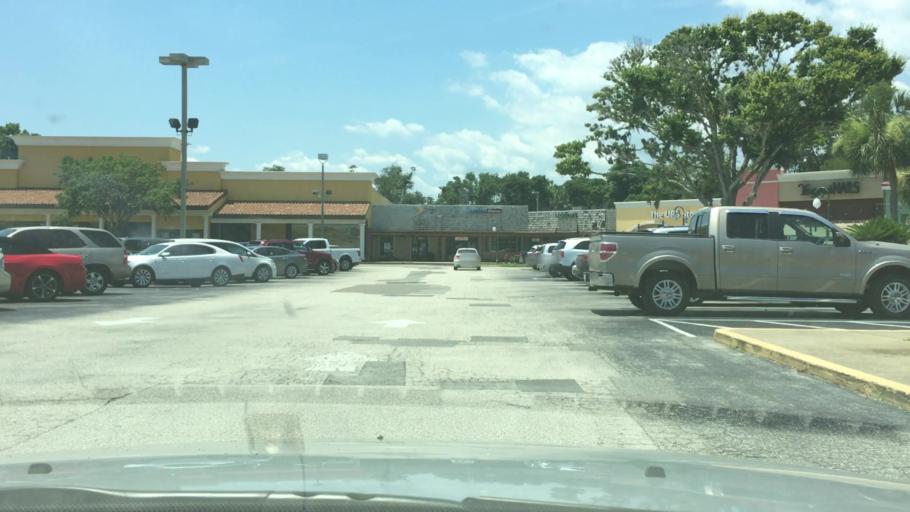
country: US
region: Florida
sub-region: Volusia County
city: Ormond Beach
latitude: 29.2837
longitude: -81.0836
